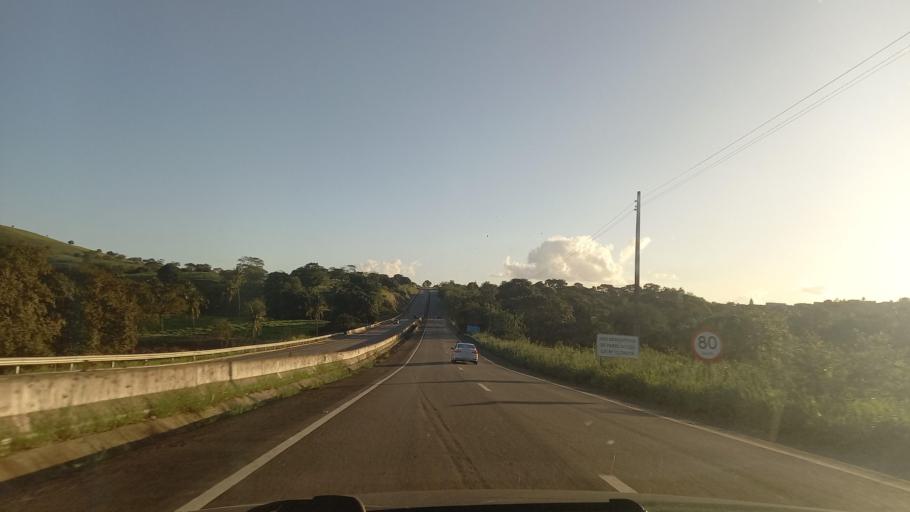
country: BR
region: Alagoas
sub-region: Limoeiro De Anadia
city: Limoeiro de Anadia
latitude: -9.7394
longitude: -36.4934
